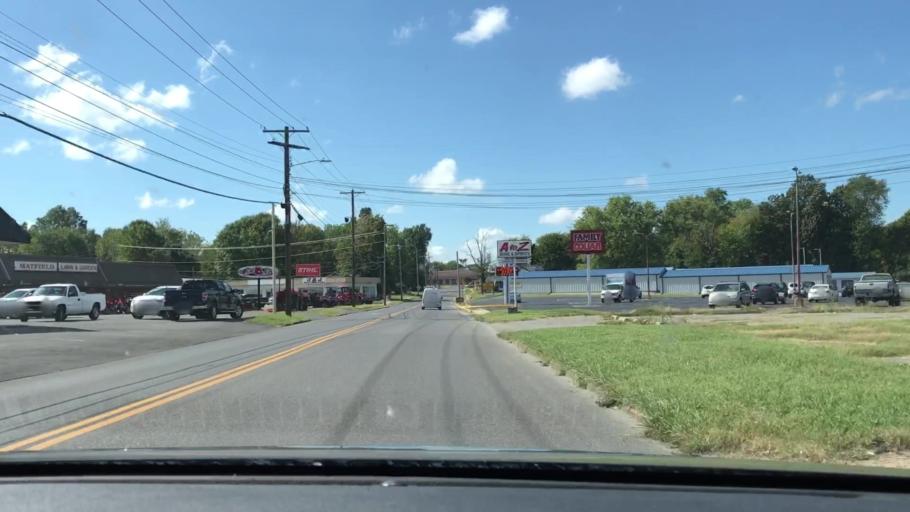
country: US
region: Kentucky
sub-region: Graves County
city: Mayfield
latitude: 36.7436
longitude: -88.6271
